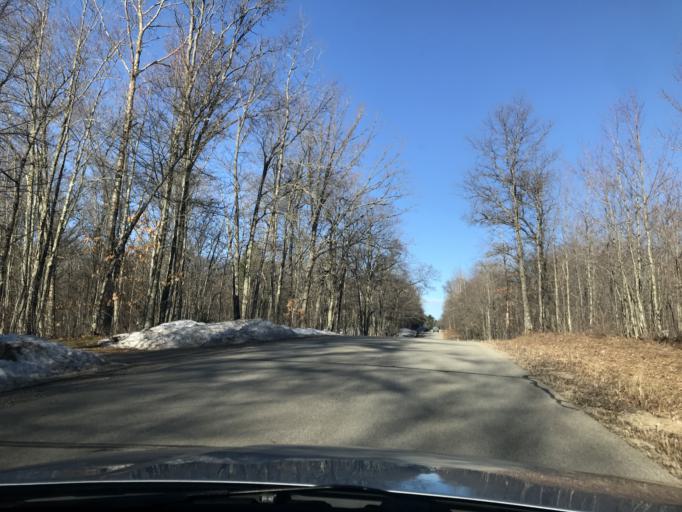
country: US
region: Wisconsin
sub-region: Marinette County
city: Niagara
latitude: 45.3904
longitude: -88.0720
